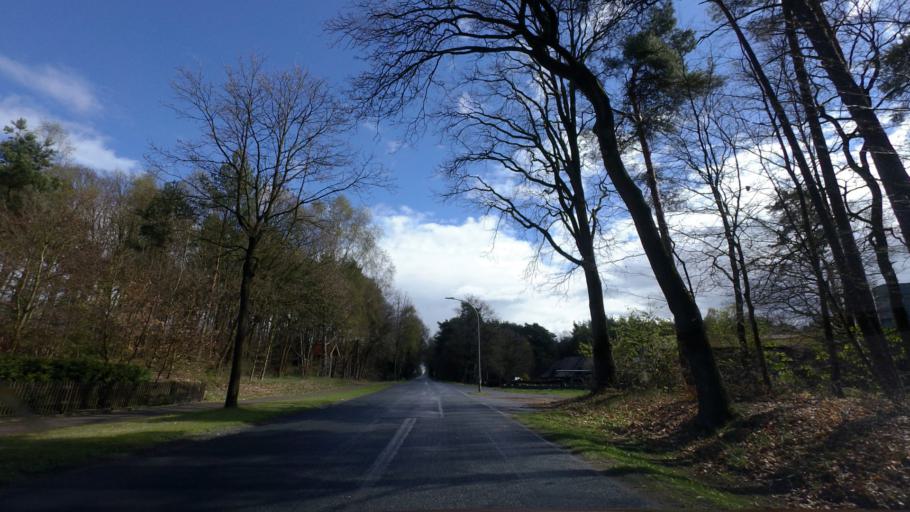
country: DE
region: Lower Saxony
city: Fintel
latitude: 53.1116
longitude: 9.7010
